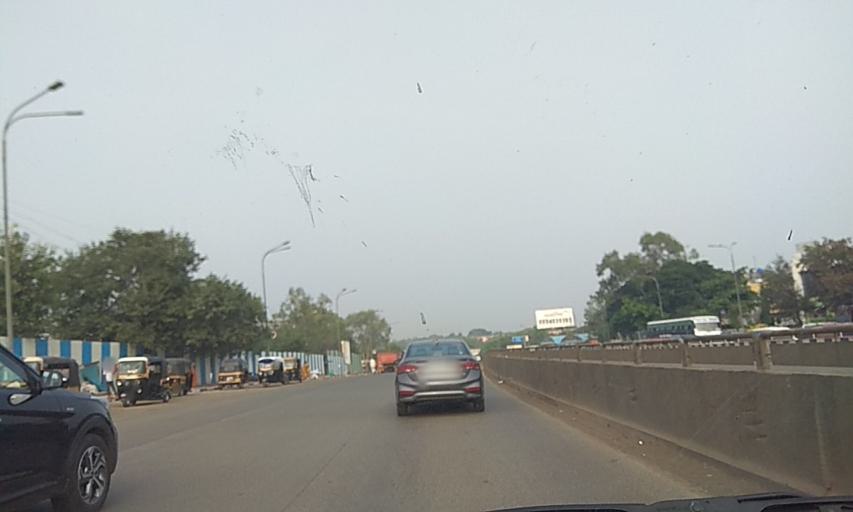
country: IN
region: Maharashtra
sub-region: Pune Division
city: Lohogaon
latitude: 18.5625
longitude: 73.9372
